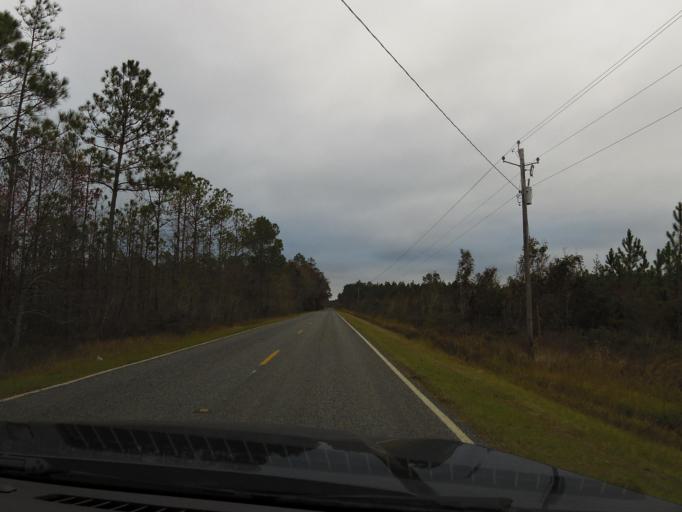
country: US
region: Georgia
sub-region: Charlton County
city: Folkston
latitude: 30.8763
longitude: -82.0491
